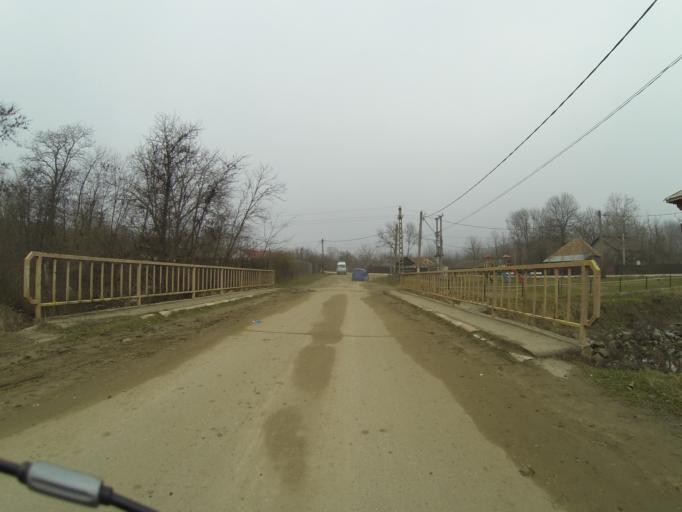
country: RO
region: Mehedinti
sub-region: Comuna Balacita
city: Gvardinita
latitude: 44.3993
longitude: 23.1450
